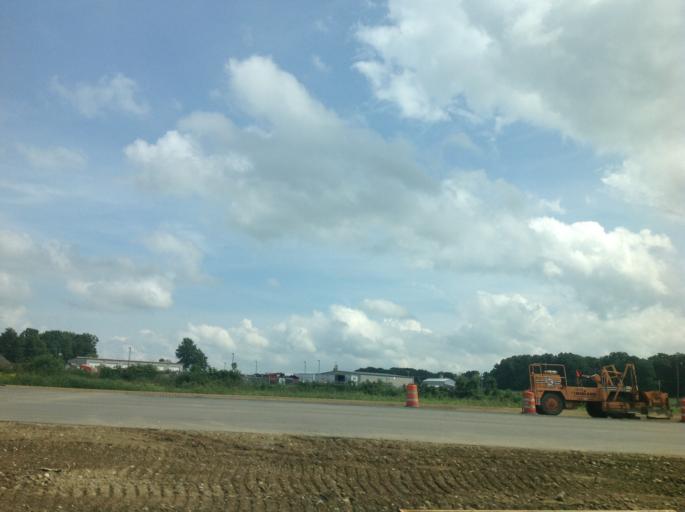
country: US
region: Ohio
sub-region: Delaware County
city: Ashley
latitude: 40.3747
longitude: -82.8289
